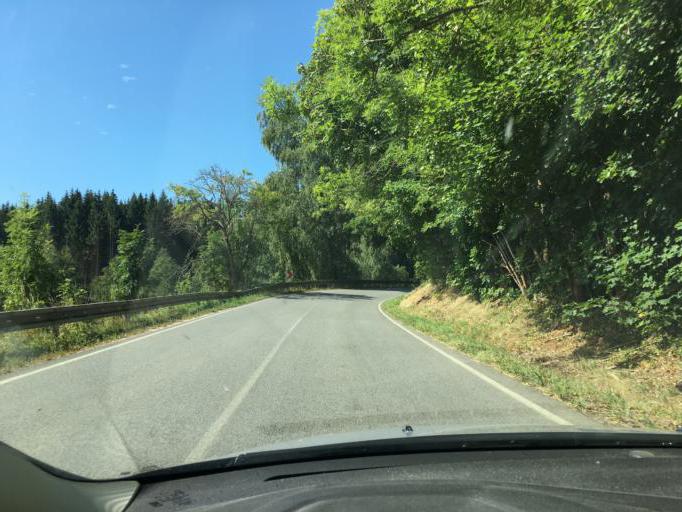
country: CZ
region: Liberecky
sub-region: Okres Semily
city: Ponikla
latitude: 50.6469
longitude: 15.4341
